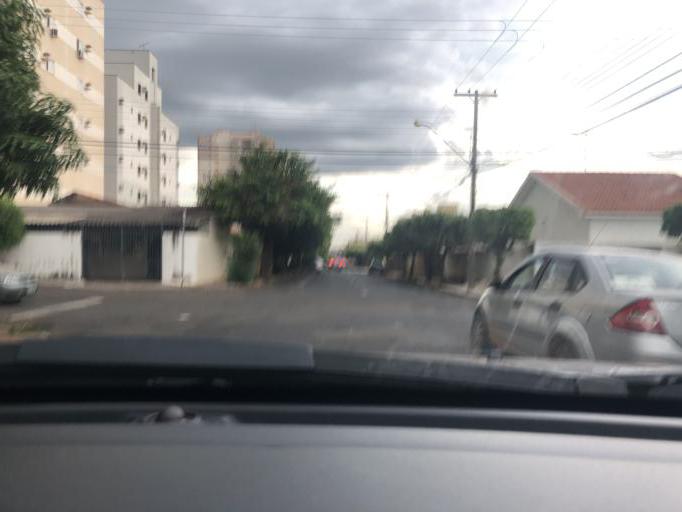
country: BR
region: Sao Paulo
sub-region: Sao Jose Do Rio Preto
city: Sao Jose do Rio Preto
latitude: -20.8403
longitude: -49.3849
